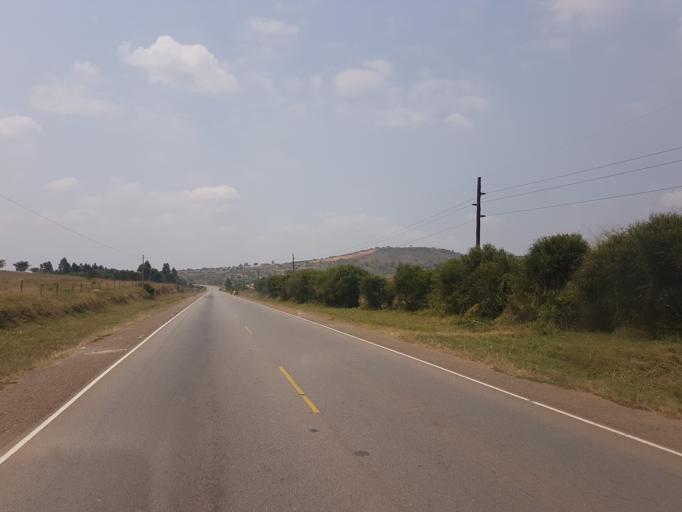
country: UG
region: Western Region
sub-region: Mbarara District
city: Mbarara
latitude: -0.5053
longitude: 30.8456
